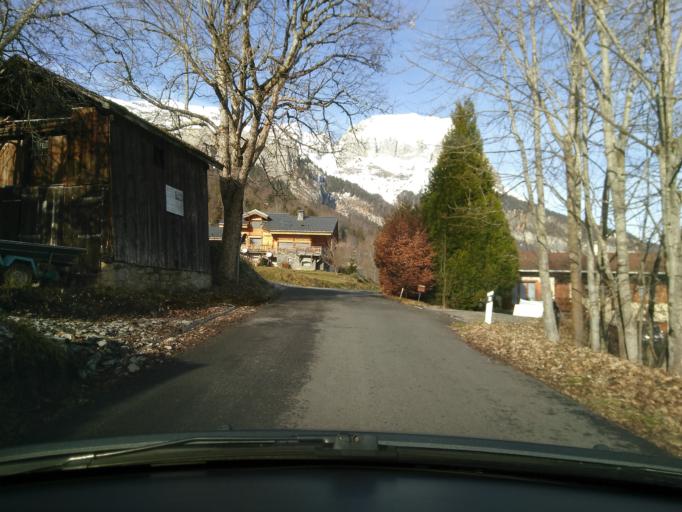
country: FR
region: Rhone-Alpes
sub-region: Departement de la Haute-Savoie
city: Sallanches
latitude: 45.9544
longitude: 6.6137
